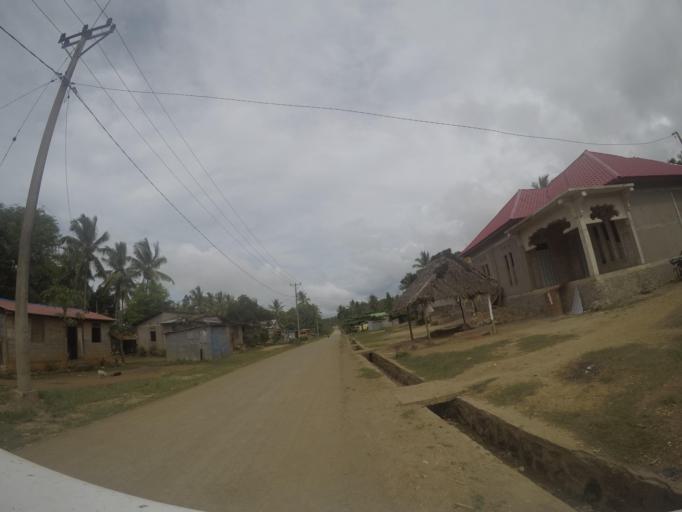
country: TL
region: Lautem
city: Lospalos
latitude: -8.5058
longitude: 126.9730
